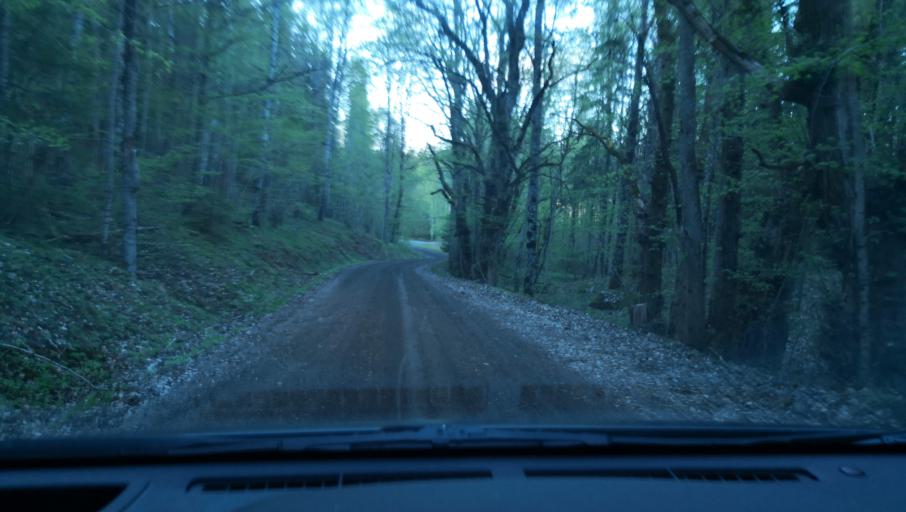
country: SE
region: OErebro
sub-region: Askersunds Kommun
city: Asbro
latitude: 58.8741
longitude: 15.1445
